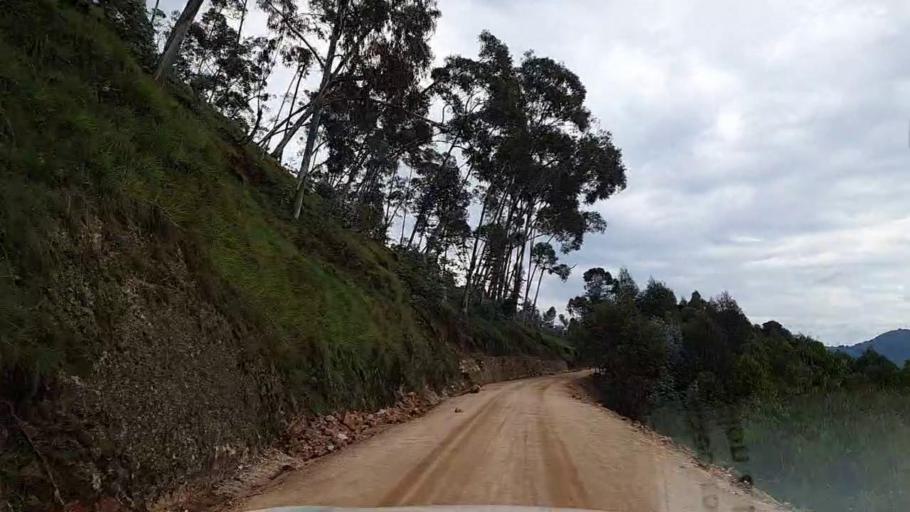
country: RW
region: Southern Province
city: Nzega
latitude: -2.3764
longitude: 29.4492
